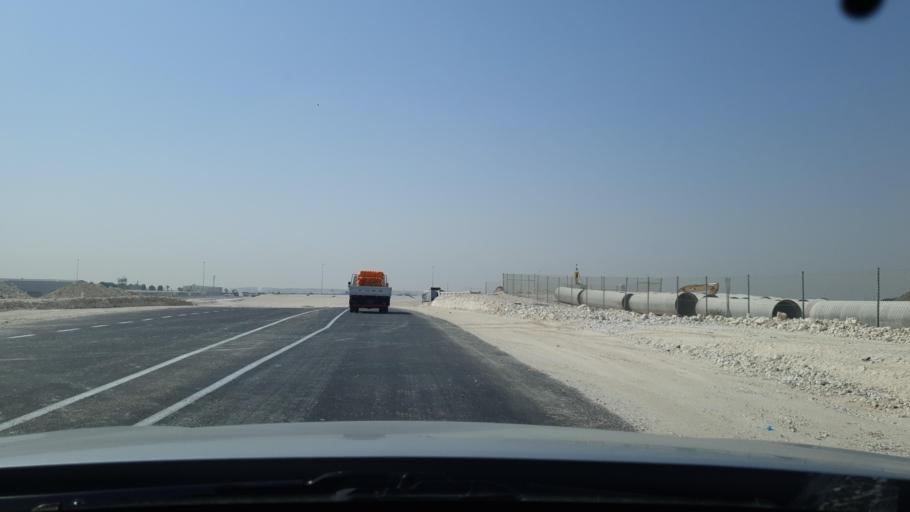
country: QA
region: Baladiyat ad Dawhah
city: Doha
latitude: 25.2269
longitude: 51.5205
